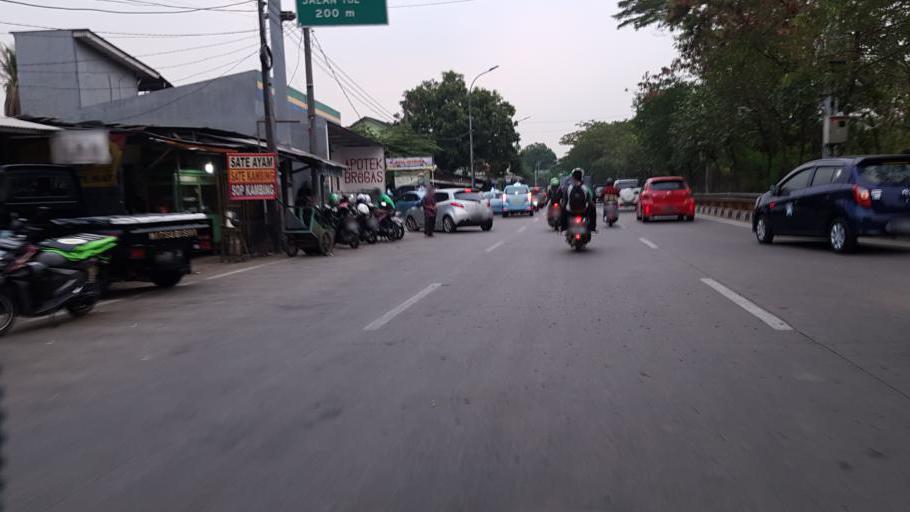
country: ID
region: West Java
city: Cileungsir
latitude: -6.3093
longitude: 106.8986
